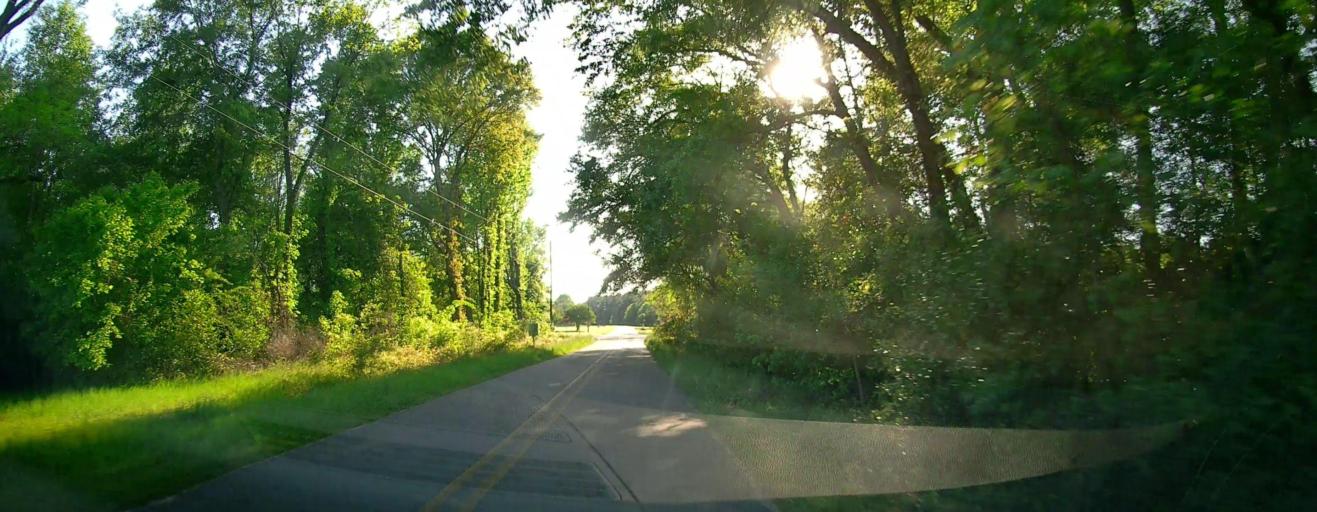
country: US
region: Georgia
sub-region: Macon County
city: Oglethorpe
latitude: 32.2908
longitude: -84.0743
